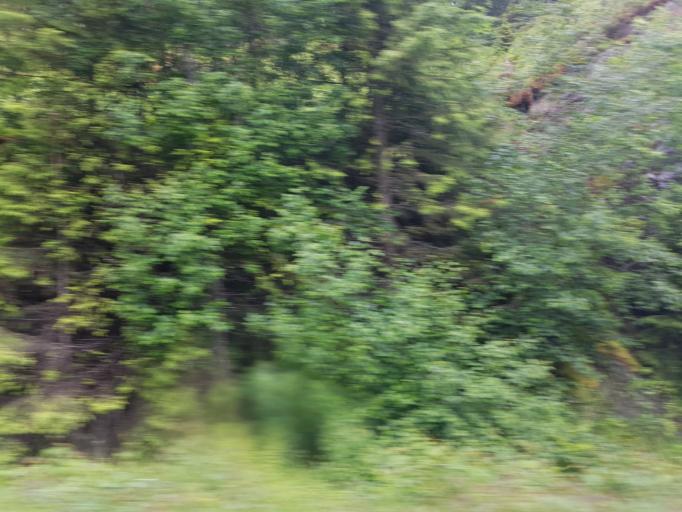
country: NO
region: Sor-Trondelag
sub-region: Selbu
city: Mebonden
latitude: 63.3629
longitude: 11.0755
